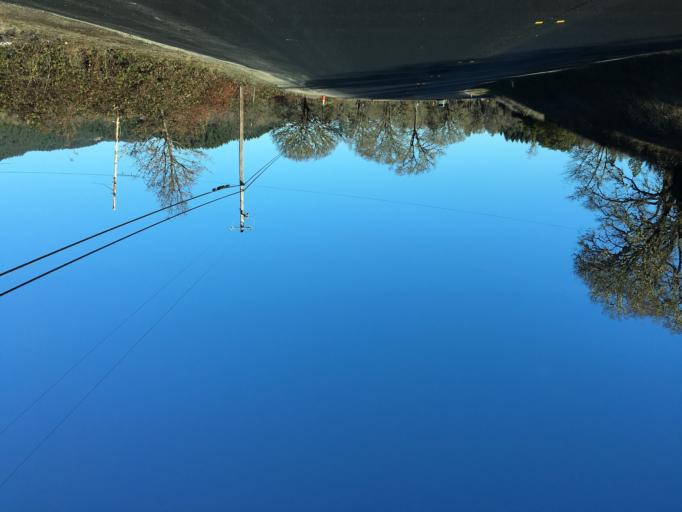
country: US
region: California
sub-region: Mendocino County
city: Laytonville
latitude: 39.6393
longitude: -123.4707
